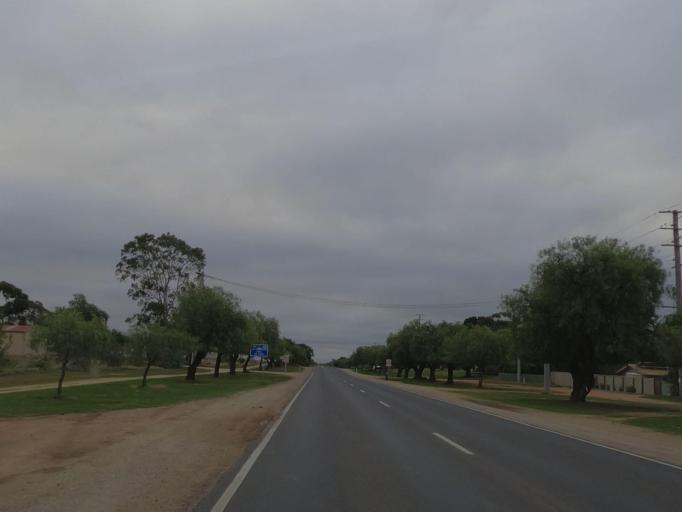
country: AU
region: Victoria
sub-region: Swan Hill
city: Swan Hill
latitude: -35.4566
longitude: 143.6296
